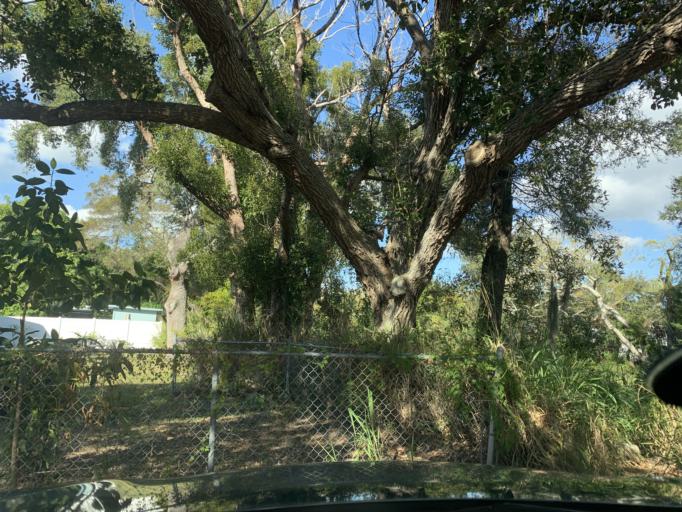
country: US
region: Florida
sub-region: Pinellas County
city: Belleair
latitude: 27.9299
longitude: -82.7928
